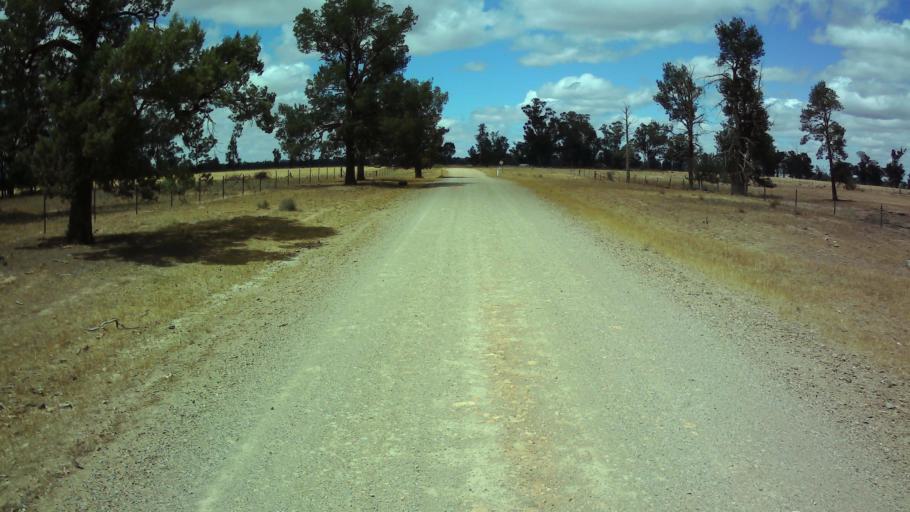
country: AU
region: New South Wales
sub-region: Weddin
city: Grenfell
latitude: -34.0161
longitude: 147.9153
